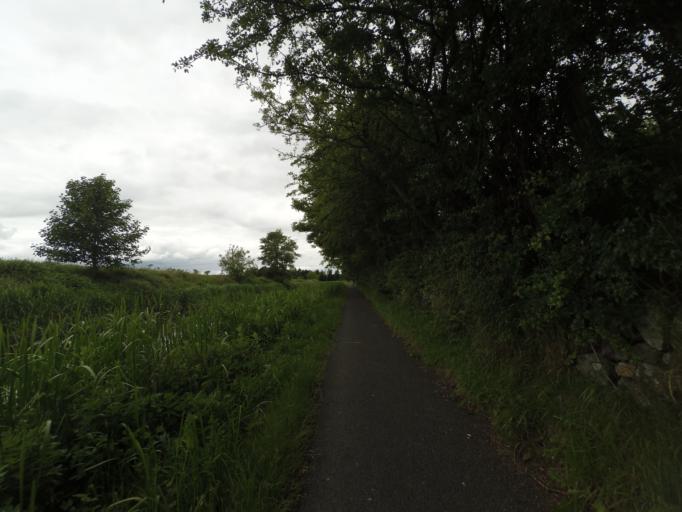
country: GB
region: Scotland
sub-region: West Lothian
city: Linlithgow
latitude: 55.9774
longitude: -3.5660
